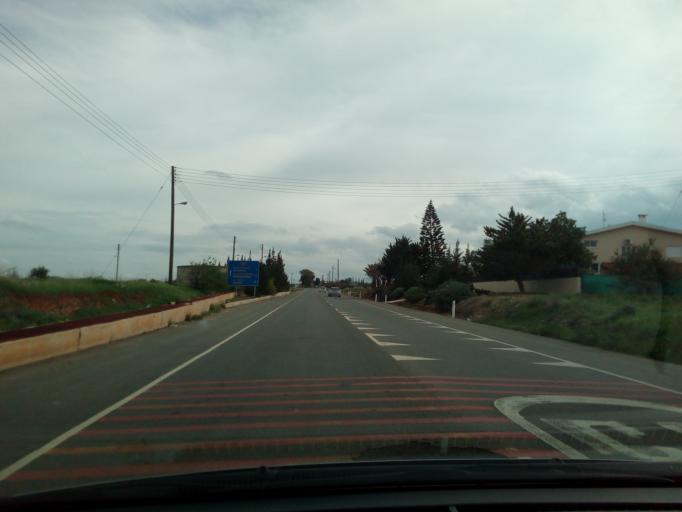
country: CY
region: Lefkosia
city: Peristerona
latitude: 35.1341
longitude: 33.0624
